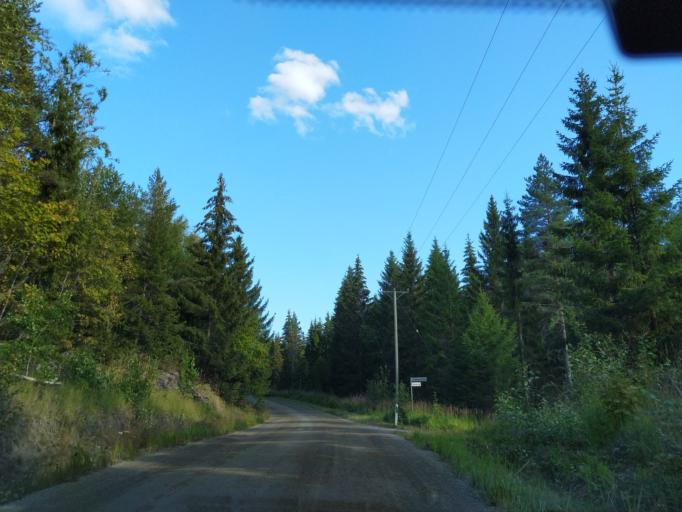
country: FI
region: Central Finland
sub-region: Jaemsae
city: Kuhmoinen
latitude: 61.6930
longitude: 24.9482
